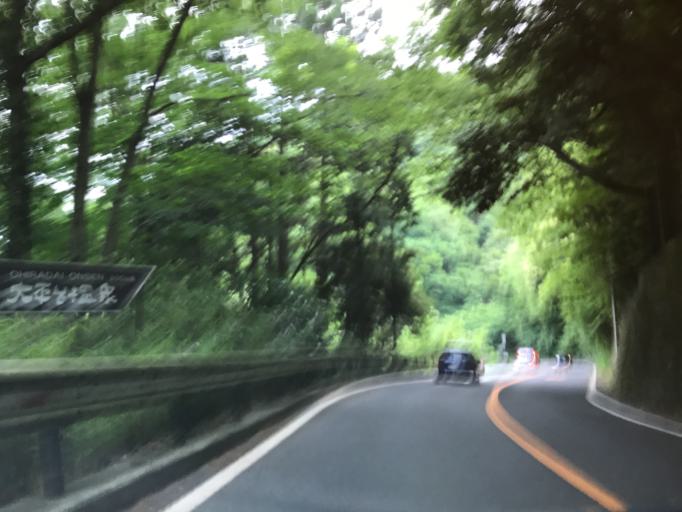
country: JP
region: Kanagawa
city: Hakone
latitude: 35.2383
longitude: 139.0691
